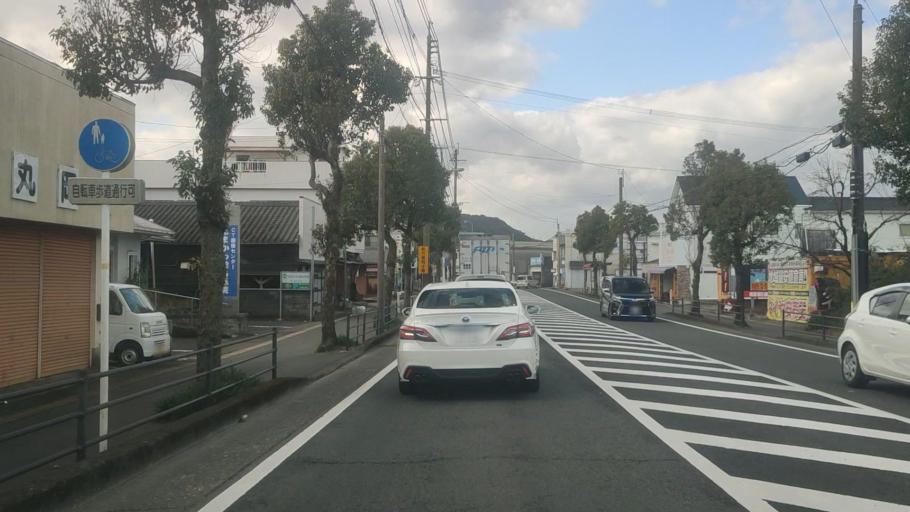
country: JP
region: Kagoshima
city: Kajiki
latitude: 31.7359
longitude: 130.6633
